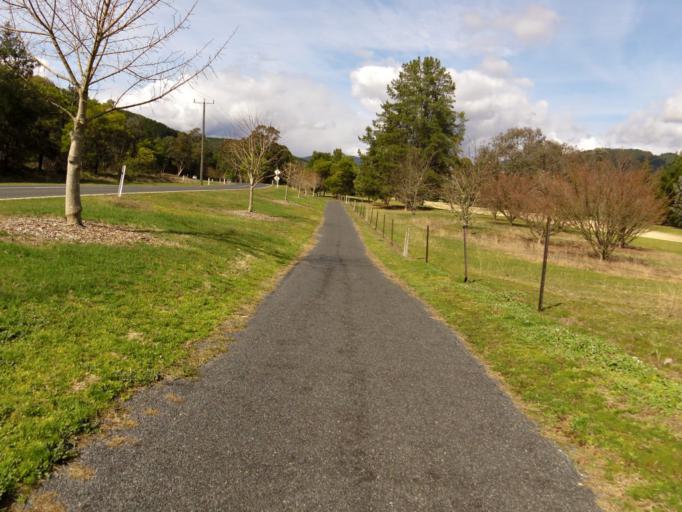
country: AU
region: Victoria
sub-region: Alpine
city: Mount Beauty
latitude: -36.7102
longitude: 146.9340
